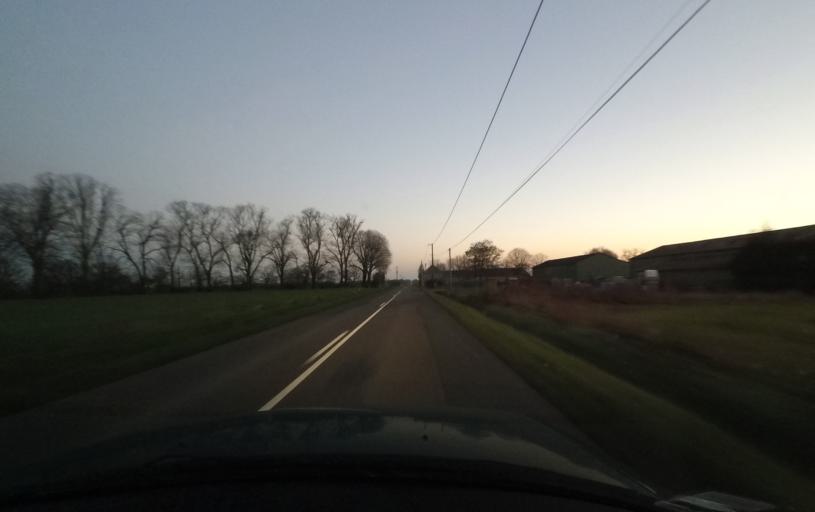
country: FR
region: Pays de la Loire
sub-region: Departement de la Mayenne
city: Meslay-du-Maine
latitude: 47.9868
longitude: -0.6116
